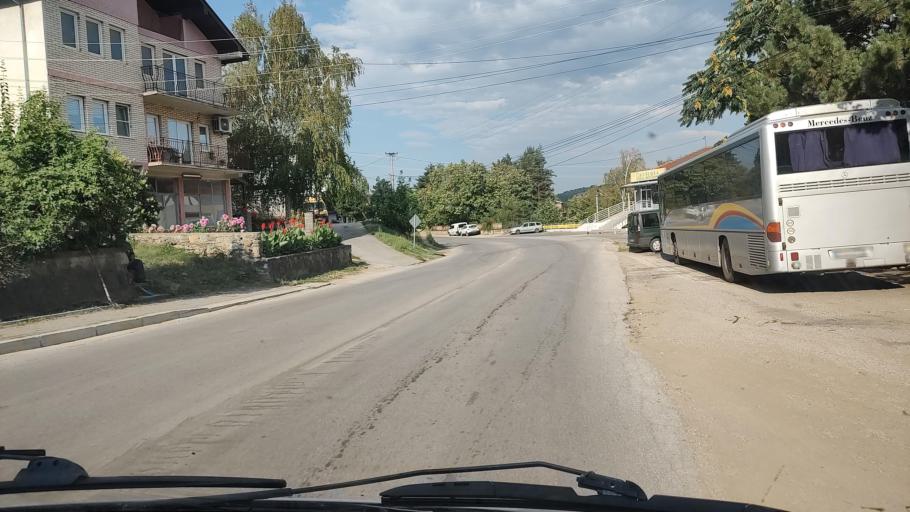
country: MK
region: Kriva Palanka
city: Kriva Palanka
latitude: 42.1951
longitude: 22.3185
